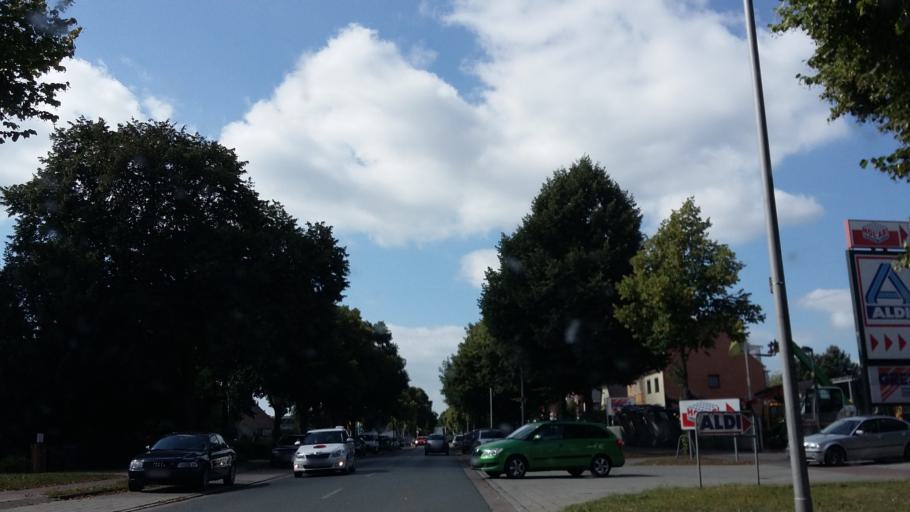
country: DE
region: Bremen
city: Bremen
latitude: 53.0407
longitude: 8.8316
